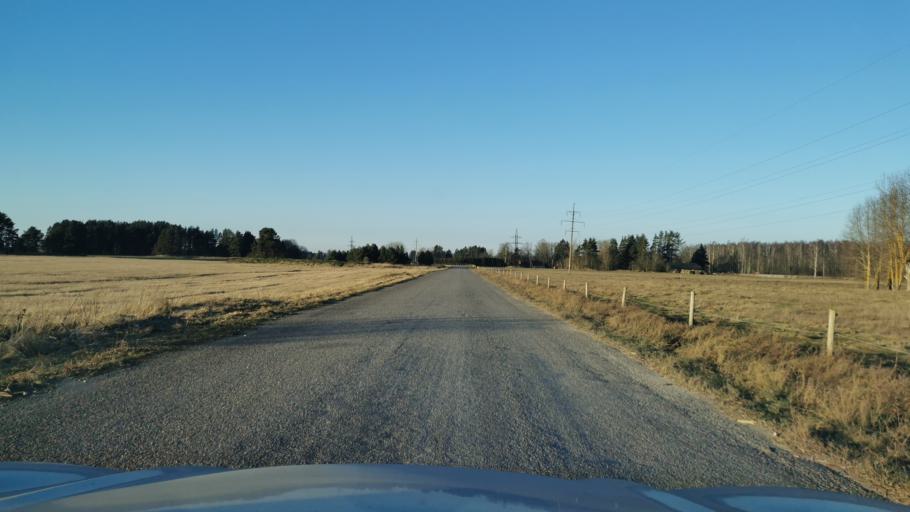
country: EE
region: Ida-Virumaa
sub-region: Puessi linn
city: Pussi
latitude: 59.3418
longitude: 27.0519
